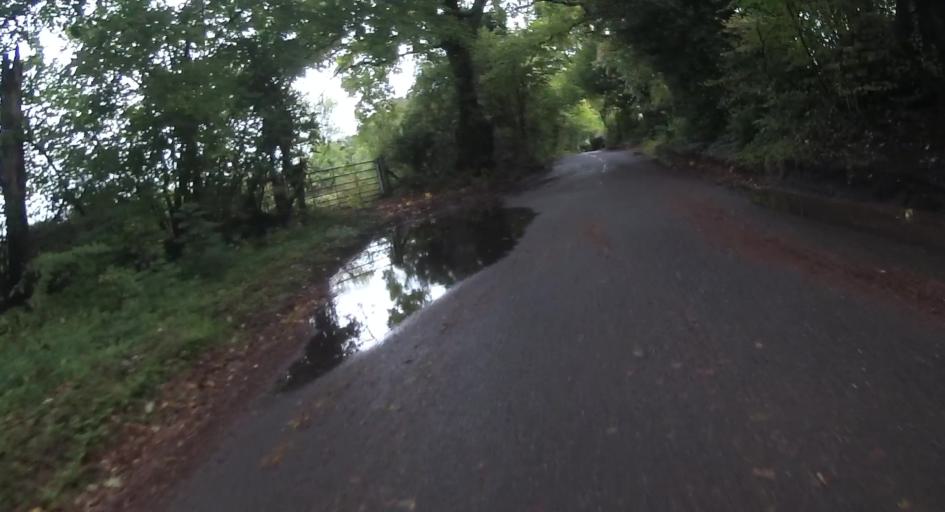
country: GB
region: England
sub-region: West Berkshire
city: Thatcham
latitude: 51.4132
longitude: -1.1805
